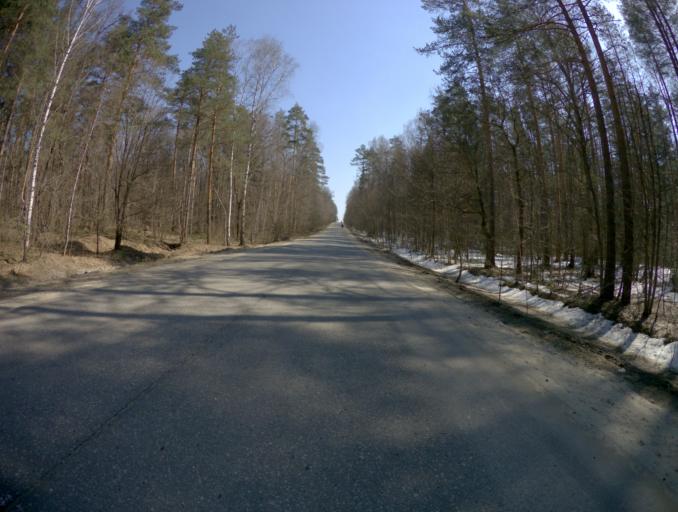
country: RU
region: Vladimir
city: Bogolyubovo
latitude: 56.1548
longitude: 40.5463
